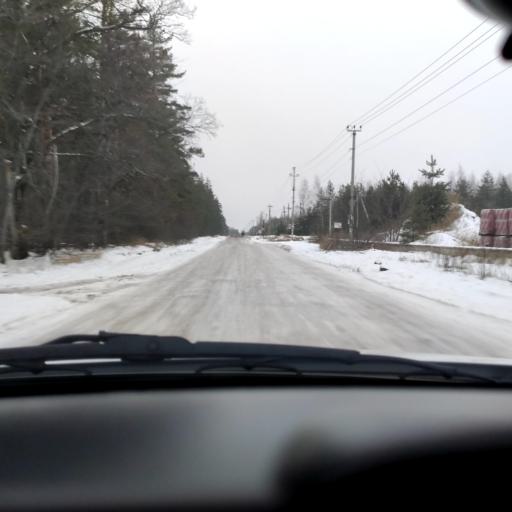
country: RU
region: Voronezj
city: Ramon'
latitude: 51.8877
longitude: 39.2517
